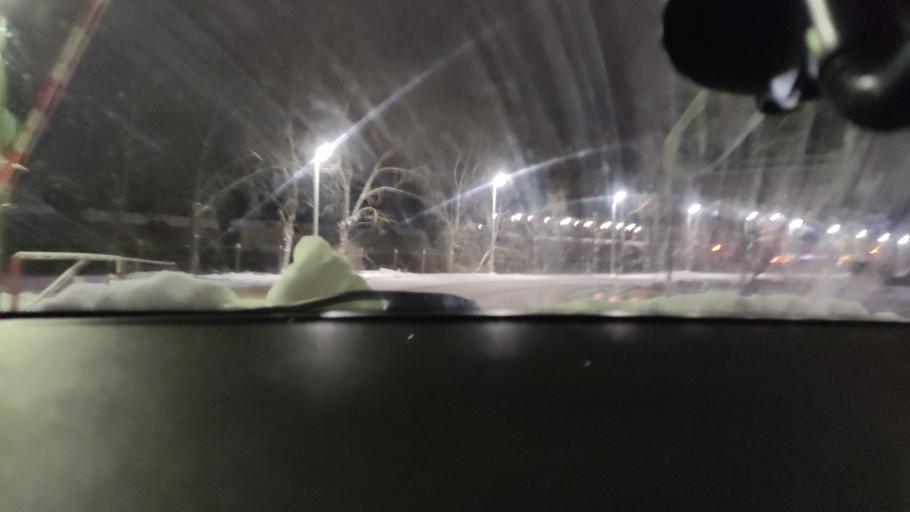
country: RU
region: Perm
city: Krasnokamsk
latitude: 58.0727
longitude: 55.7778
